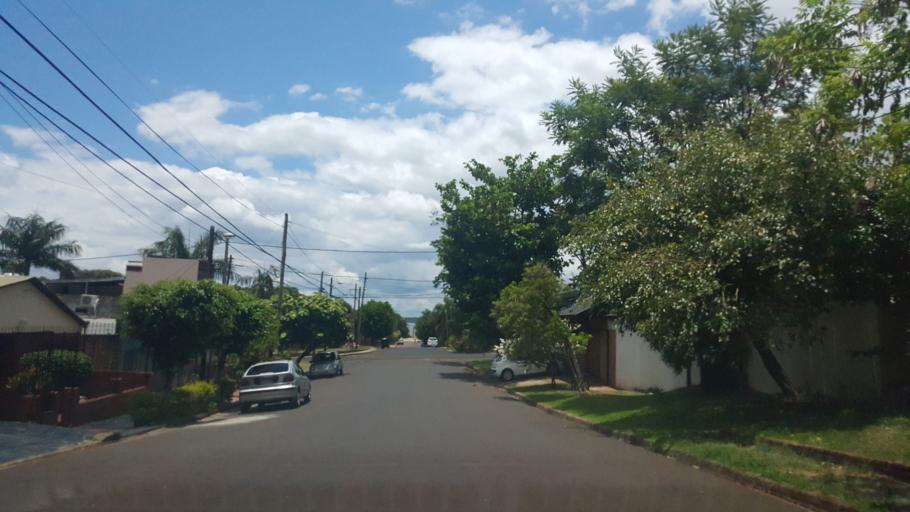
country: AR
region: Misiones
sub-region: Departamento de Capital
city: Posadas
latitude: -27.3560
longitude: -55.9010
